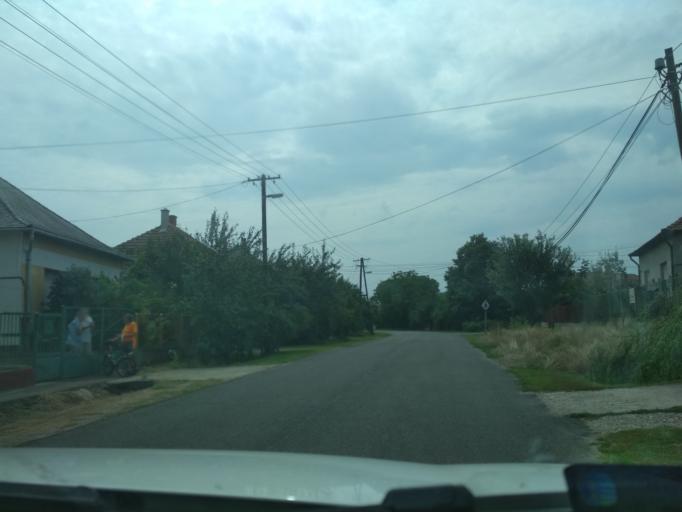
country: HU
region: Jasz-Nagykun-Szolnok
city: Tiszafured
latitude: 47.6132
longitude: 20.7535
